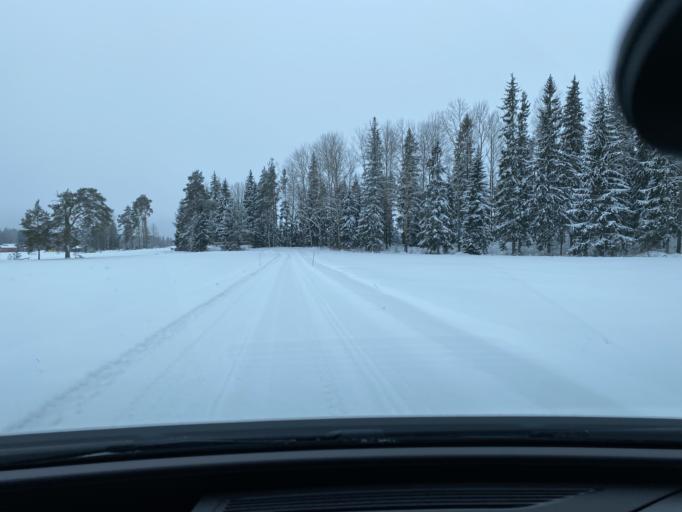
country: FI
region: Pirkanmaa
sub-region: Lounais-Pirkanmaa
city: Punkalaidun
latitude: 61.1298
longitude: 23.0904
